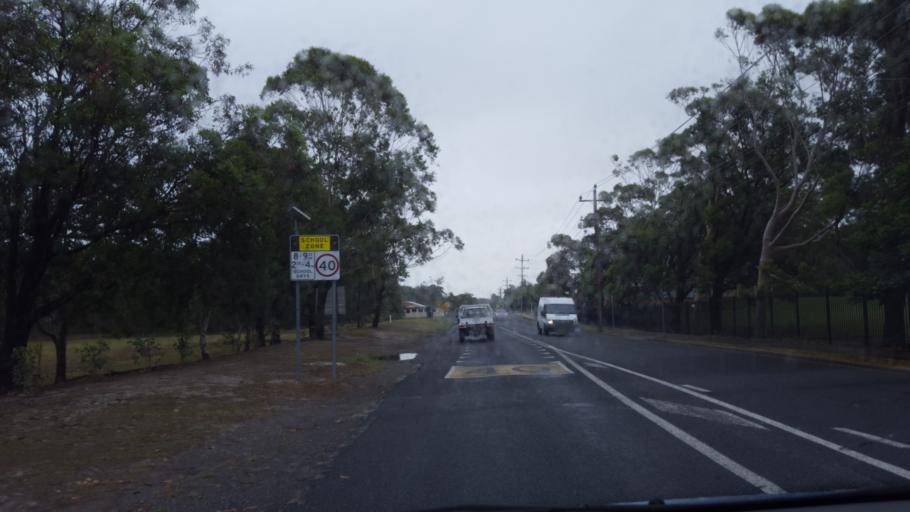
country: AU
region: New South Wales
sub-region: Port Stephens Shire
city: Anna Bay
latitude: -32.7765
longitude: 152.0919
